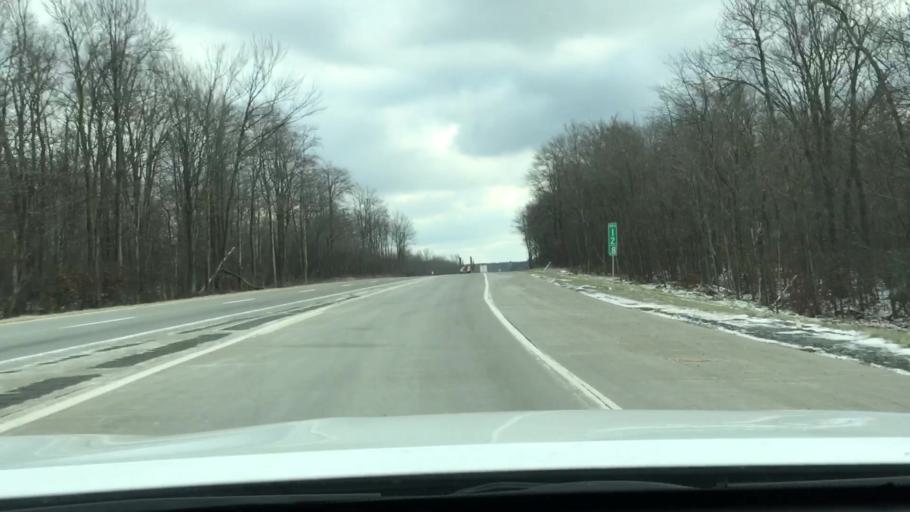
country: US
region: Pennsylvania
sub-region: Lackawanna County
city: Moscow
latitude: 41.2283
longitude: -75.4953
